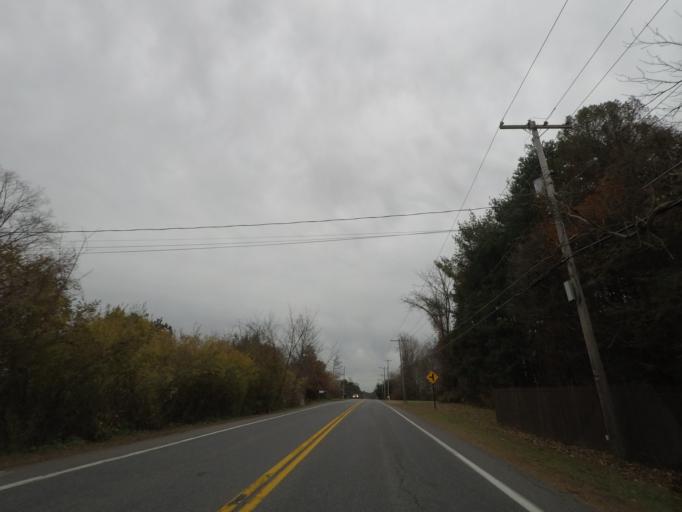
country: US
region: New York
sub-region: Saratoga County
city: Country Knolls
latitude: 42.8488
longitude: -73.8201
